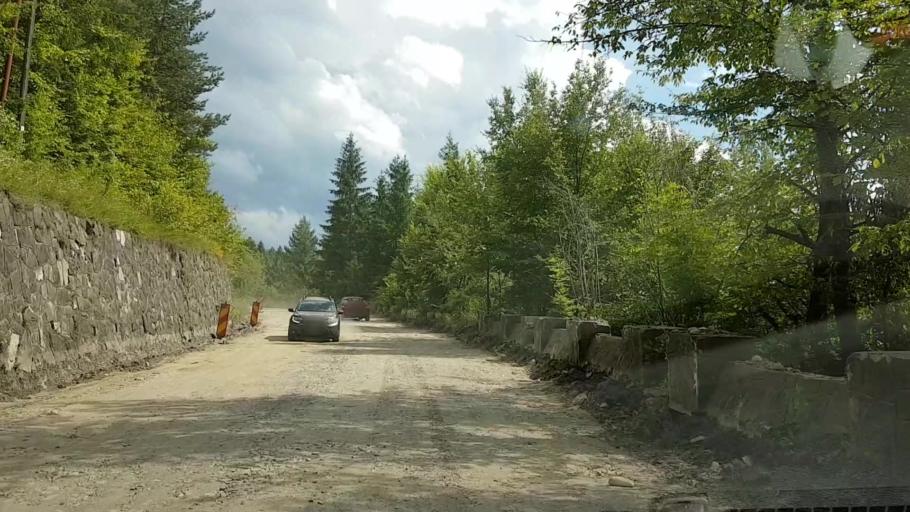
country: RO
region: Neamt
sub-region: Comuna Hangu
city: Hangu
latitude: 47.0526
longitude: 26.0384
